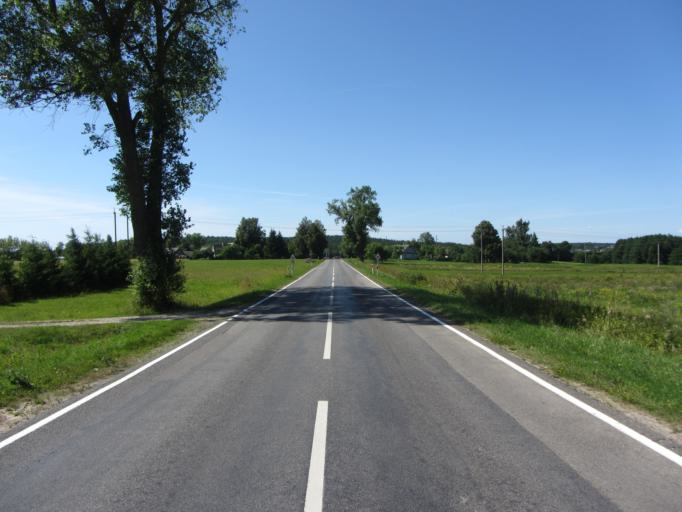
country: LT
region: Vilnius County
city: Elektrenai
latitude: 54.8471
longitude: 24.5884
